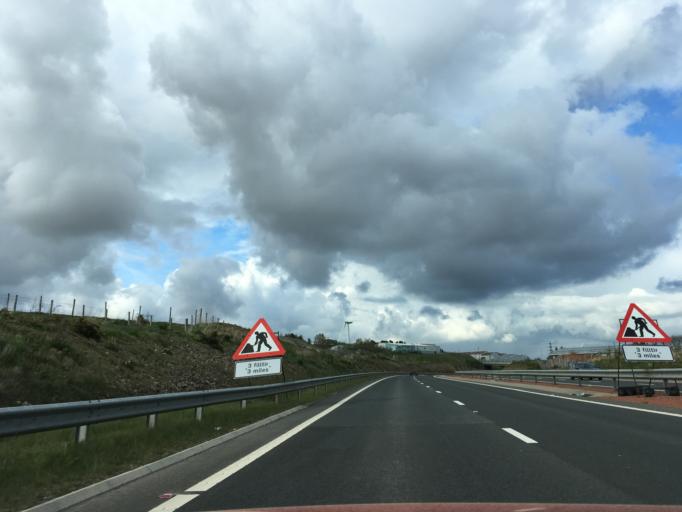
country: GB
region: Wales
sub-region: Blaenau Gwent
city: Tredegar
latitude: 51.7953
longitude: -3.2448
